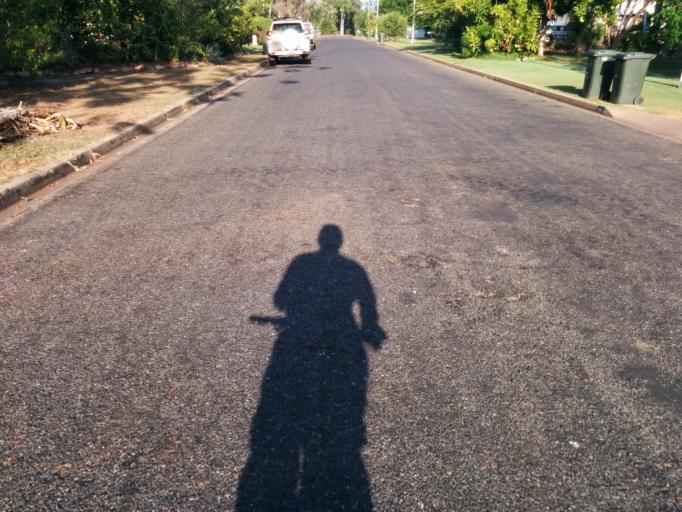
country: AU
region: Northern Territory
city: Alyangula
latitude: -13.8490
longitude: 136.4215
